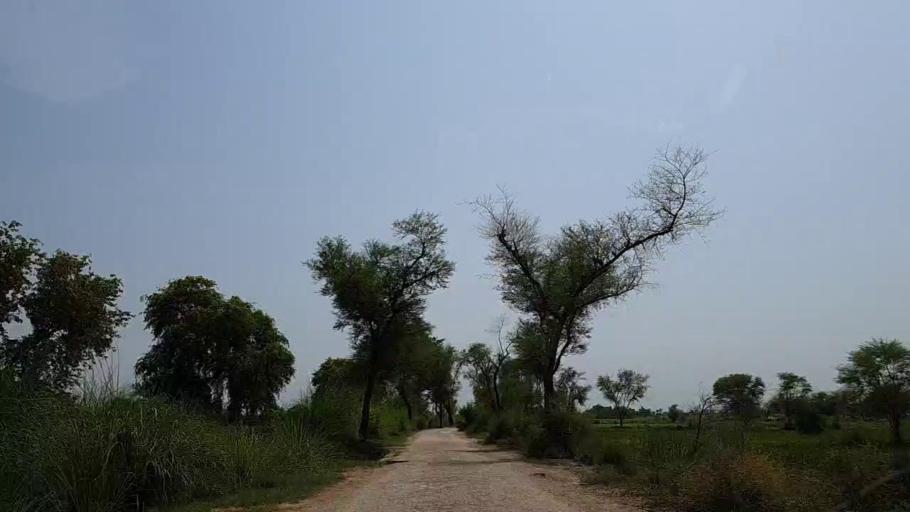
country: PK
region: Sindh
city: Adilpur
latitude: 27.9232
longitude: 69.3758
